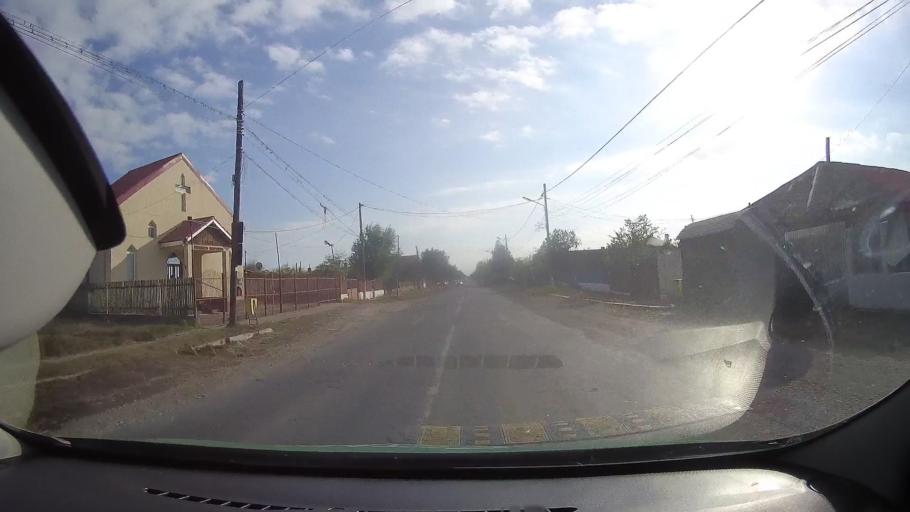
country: RO
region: Constanta
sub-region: Comuna Corbu
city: Corbu
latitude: 44.3951
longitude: 28.6619
